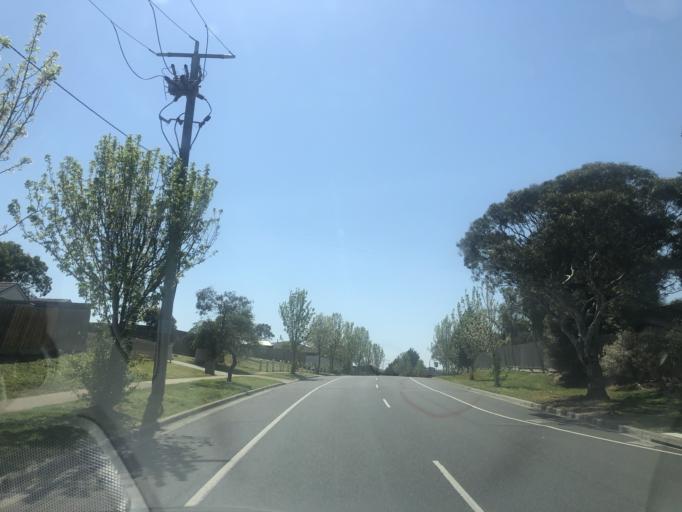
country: AU
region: Victoria
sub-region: Casey
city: Narre Warren South
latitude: -38.0419
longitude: 145.2799
